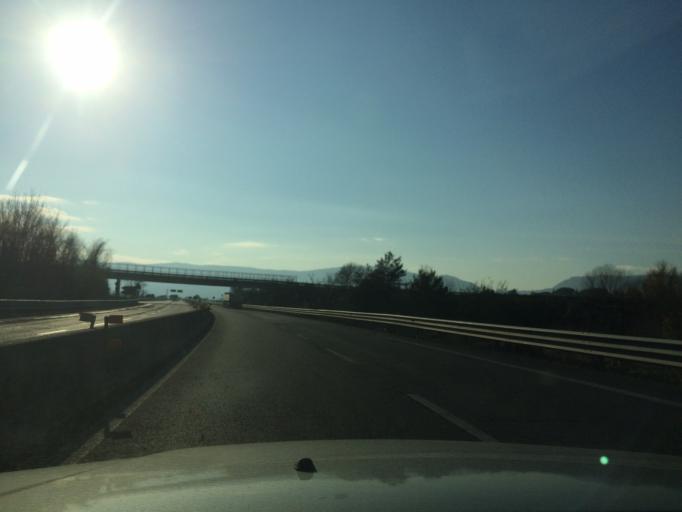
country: IT
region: Umbria
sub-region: Provincia di Terni
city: Narni Scalo
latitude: 42.5580
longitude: 12.5372
